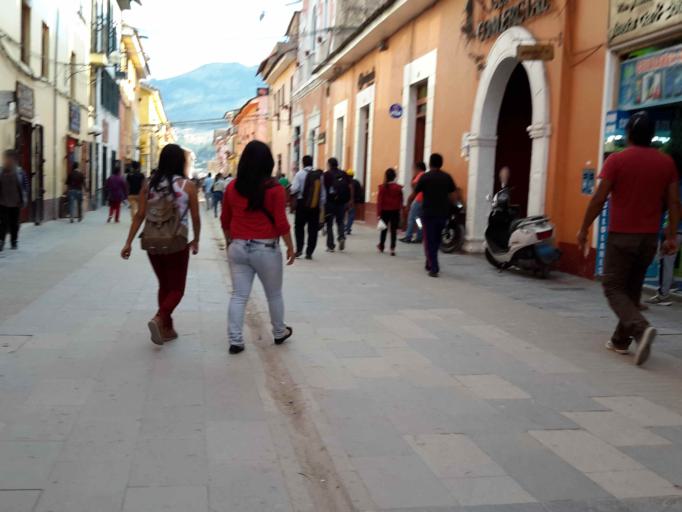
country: PE
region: Ayacucho
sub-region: Provincia de Huamanga
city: Ayacucho
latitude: -13.1582
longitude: -74.2247
